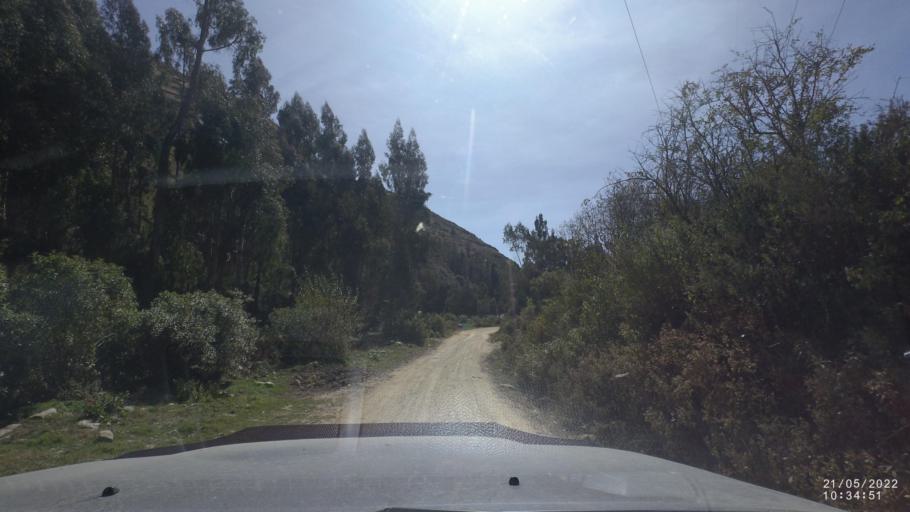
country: BO
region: Cochabamba
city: Colomi
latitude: -17.3194
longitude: -65.9300
